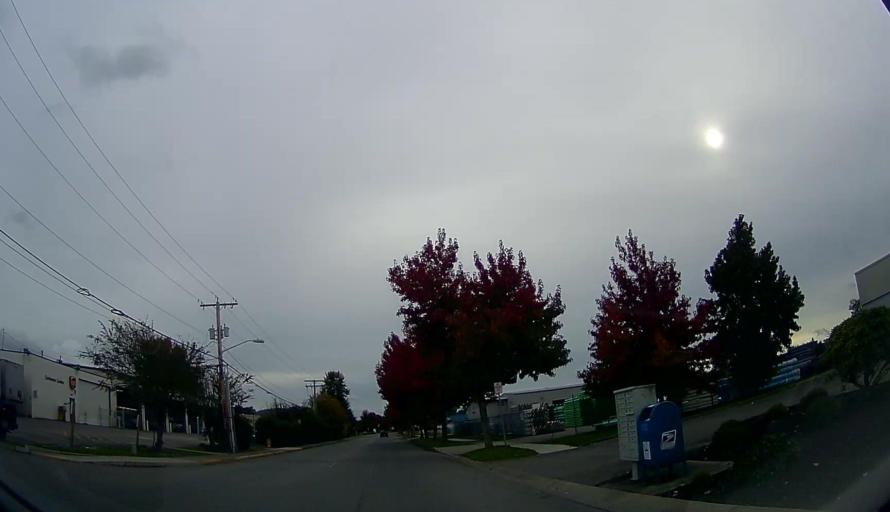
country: US
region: Washington
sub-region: Skagit County
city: Burlington
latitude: 48.4554
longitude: -122.3274
